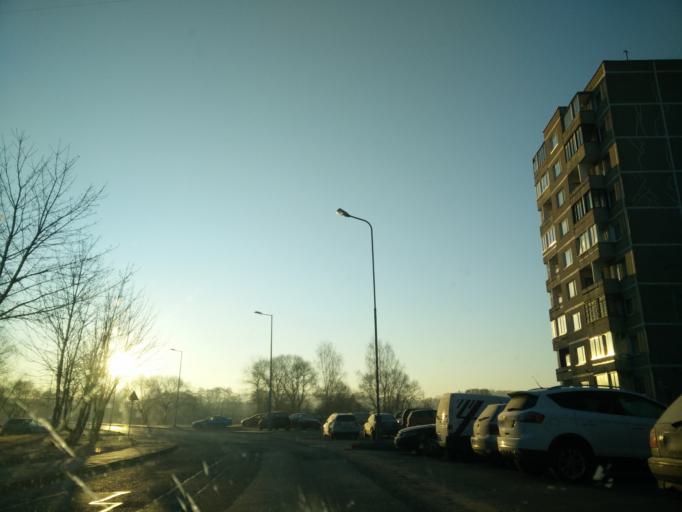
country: LT
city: Grigiskes
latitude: 54.6681
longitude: 25.1010
